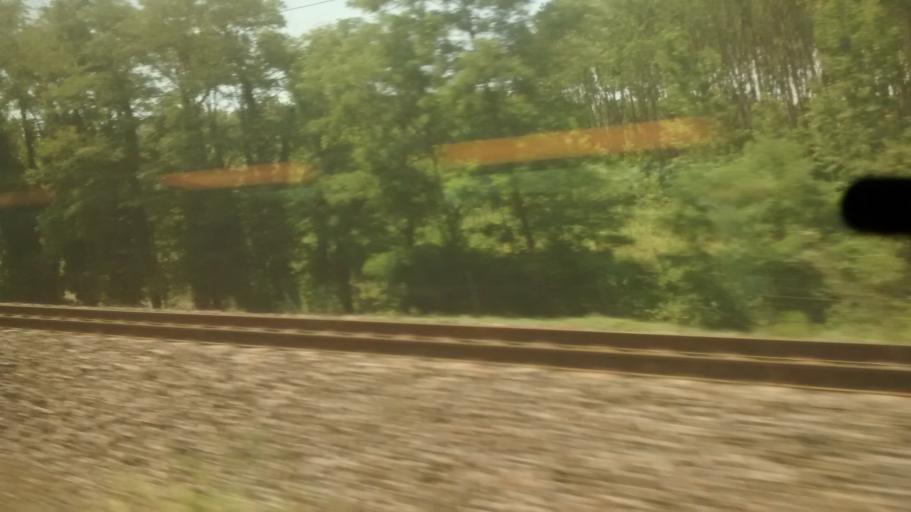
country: FR
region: Rhone-Alpes
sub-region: Departement de l'Ain
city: Grieges
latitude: 46.2479
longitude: 4.8460
